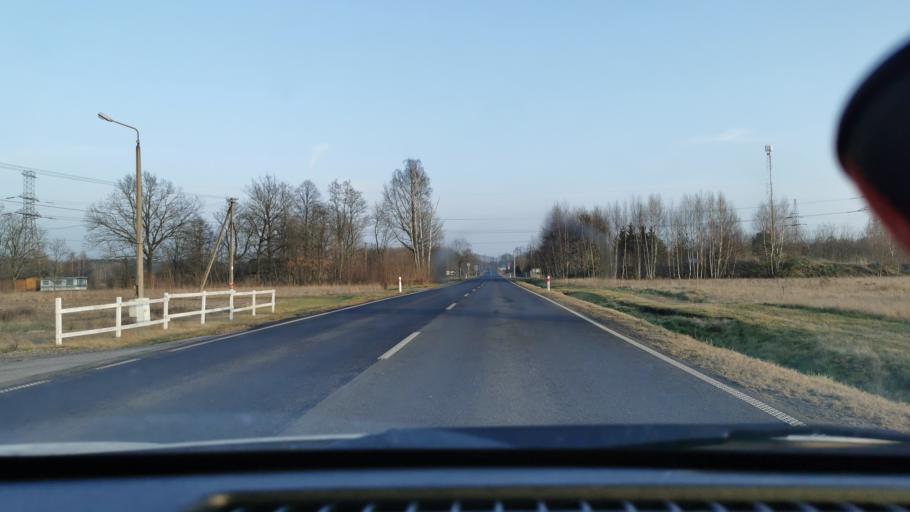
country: PL
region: Lodz Voivodeship
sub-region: Powiat belchatowski
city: Zelow
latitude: 51.5273
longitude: 19.2919
